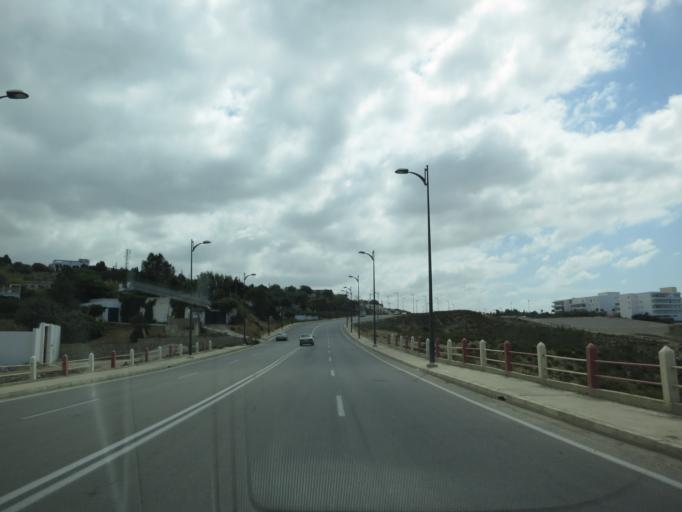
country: MA
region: Tanger-Tetouan
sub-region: Tanger-Assilah
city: Tangier
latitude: 35.8060
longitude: -5.7430
